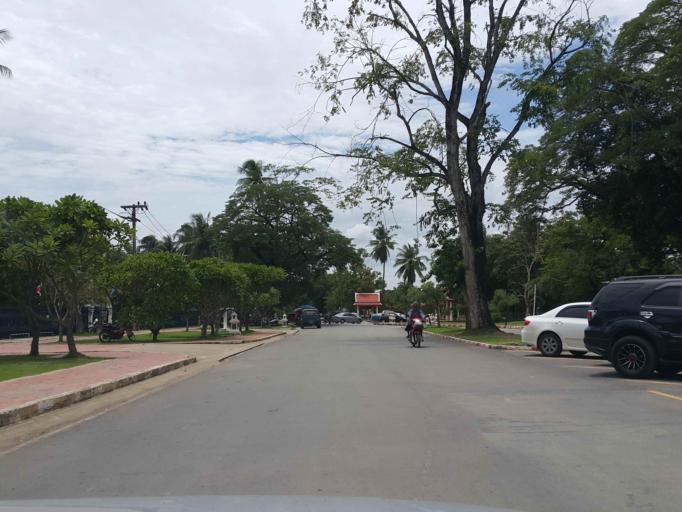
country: TH
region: Sukhothai
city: Ban Na
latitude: 17.0181
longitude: 99.7068
